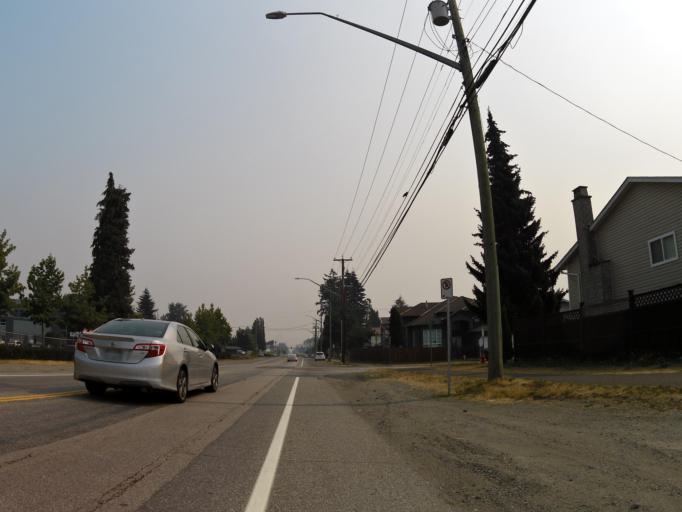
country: CA
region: British Columbia
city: Delta
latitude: 49.1482
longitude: -122.8726
